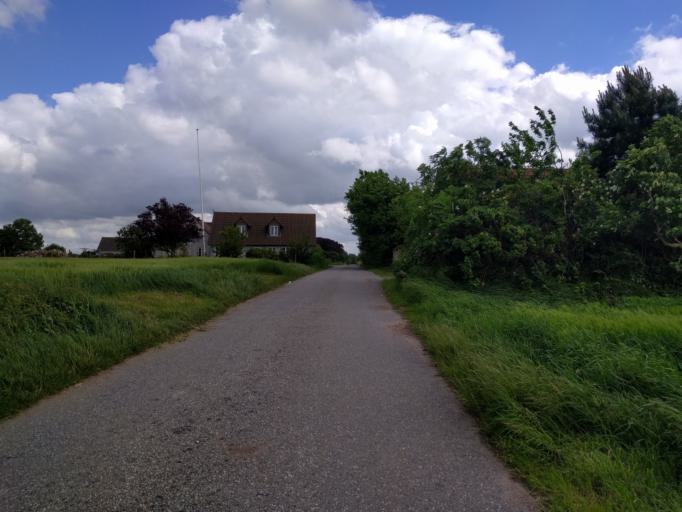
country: DK
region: South Denmark
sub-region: Odense Kommune
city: Bullerup
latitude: 55.4591
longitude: 10.5001
